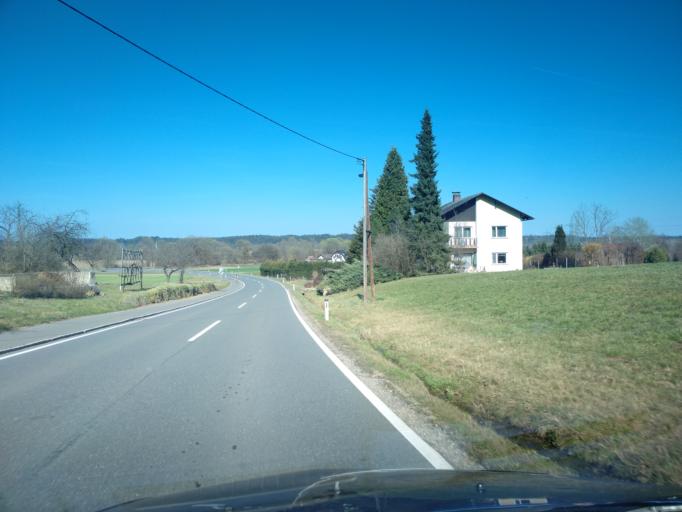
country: AT
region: Styria
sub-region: Politischer Bezirk Deutschlandsberg
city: Preding
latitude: 46.8971
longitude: 15.4067
